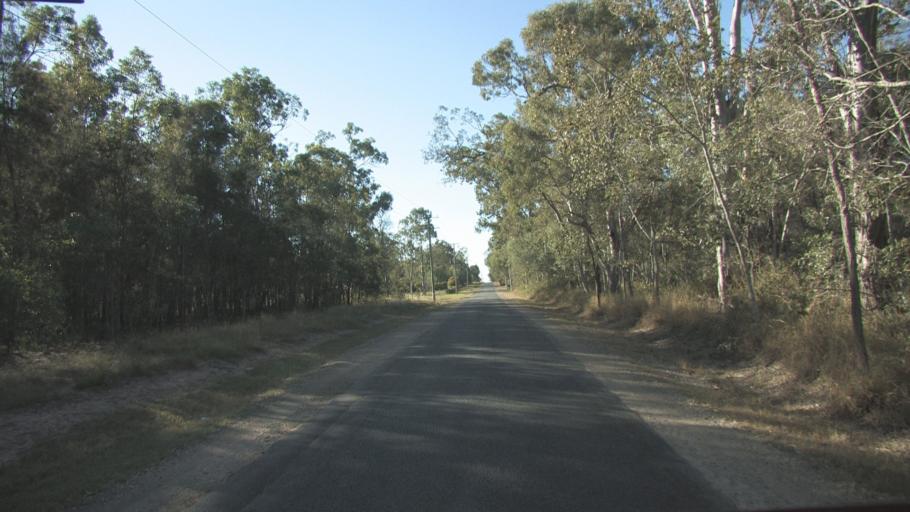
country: AU
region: Queensland
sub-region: Logan
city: North Maclean
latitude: -27.7867
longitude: 153.0388
